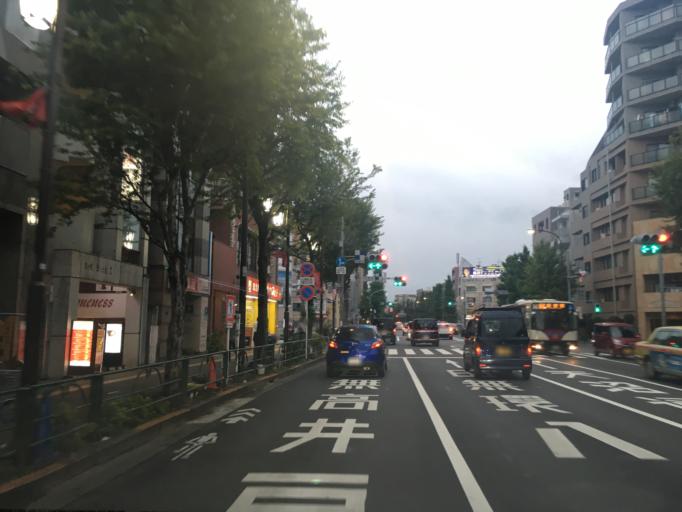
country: JP
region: Tokyo
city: Musashino
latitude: 35.7075
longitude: 139.6159
